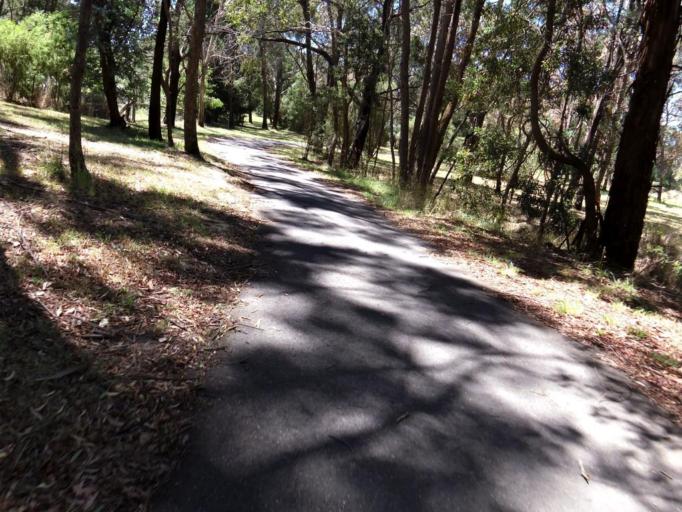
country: AU
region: Victoria
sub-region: Hume
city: Sunbury
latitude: -37.3559
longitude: 144.5398
